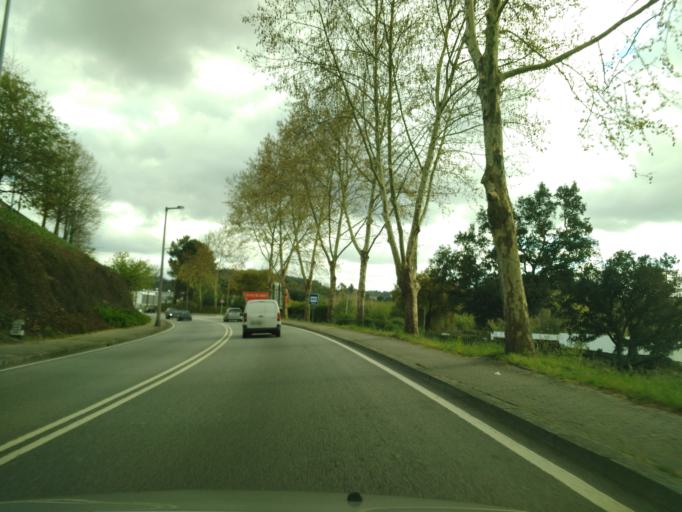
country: PT
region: Braga
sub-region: Guimaraes
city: Urgeses
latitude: 41.4262
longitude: -8.3049
